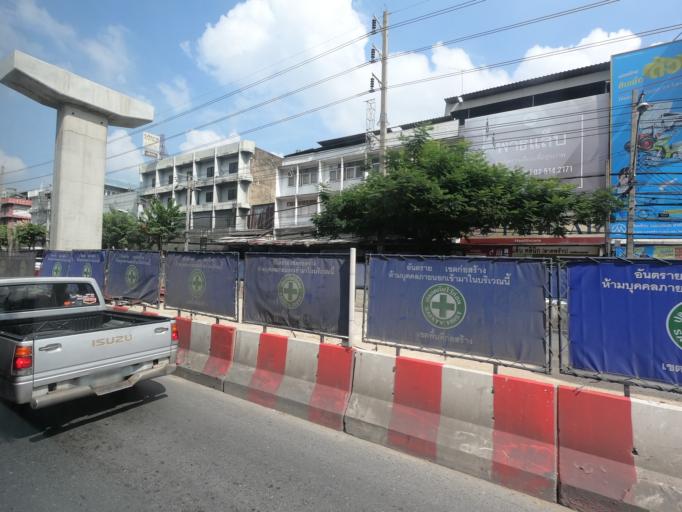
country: TH
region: Bangkok
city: Lat Phrao
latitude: 13.7934
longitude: 100.5963
